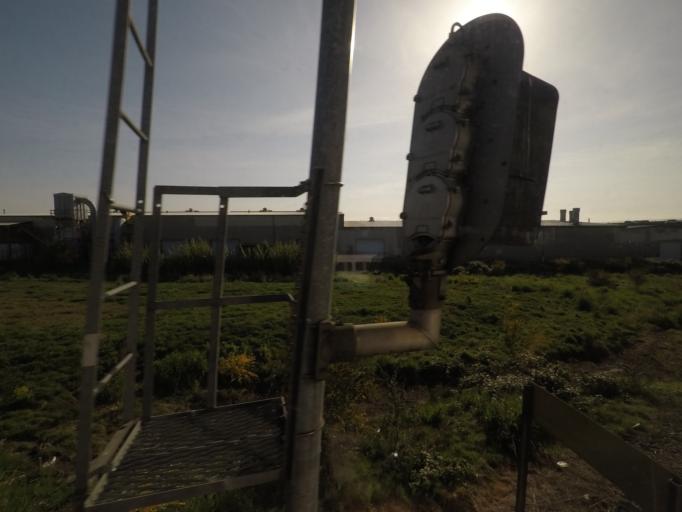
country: US
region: Washington
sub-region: Snohomish County
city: Everett
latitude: 47.9720
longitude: -122.1955
